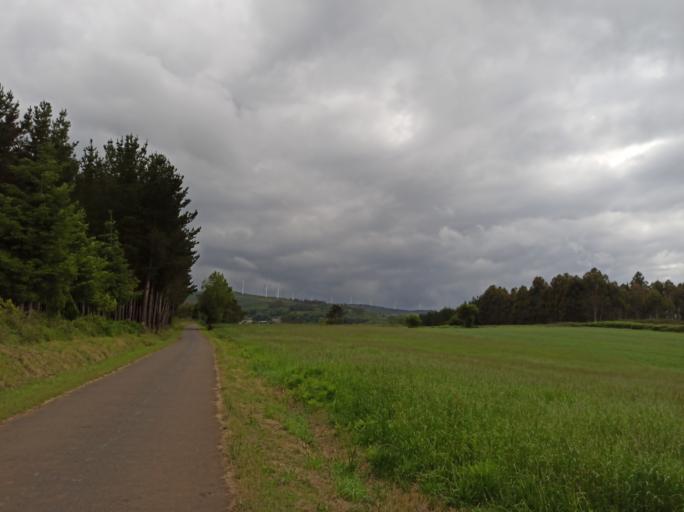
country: ES
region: Galicia
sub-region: Provincia de Pontevedra
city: Silleda
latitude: 42.7639
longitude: -8.1603
